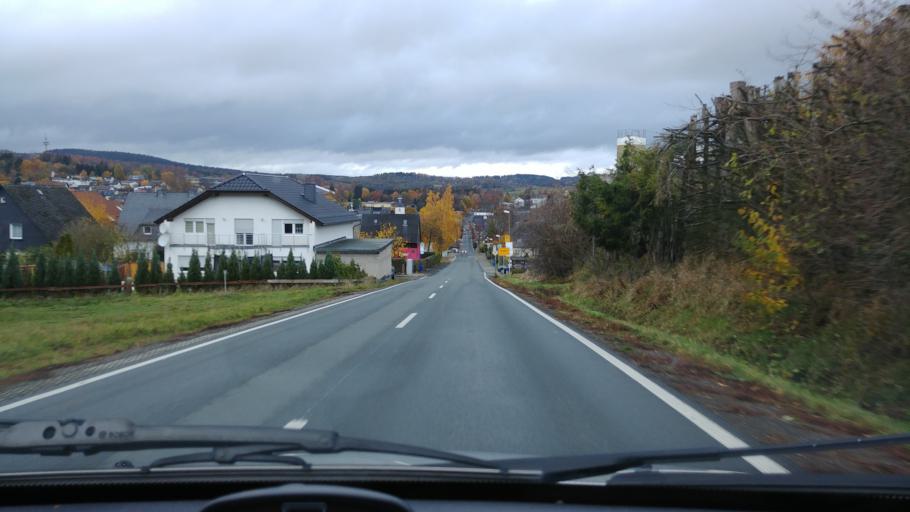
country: DE
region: Hesse
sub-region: Regierungsbezirk Giessen
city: Driedorf
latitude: 50.6296
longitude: 8.1903
